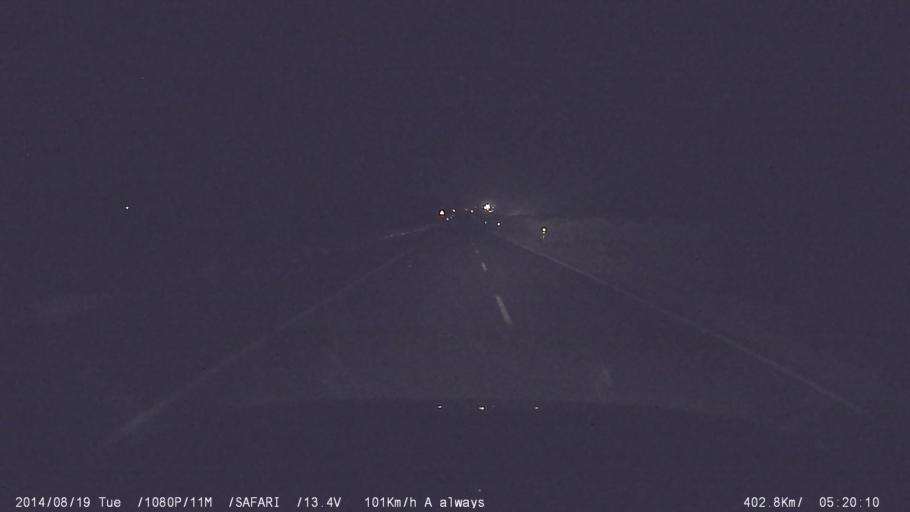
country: IN
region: Tamil Nadu
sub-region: Salem
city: Konganapuram
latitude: 11.5371
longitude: 77.9667
